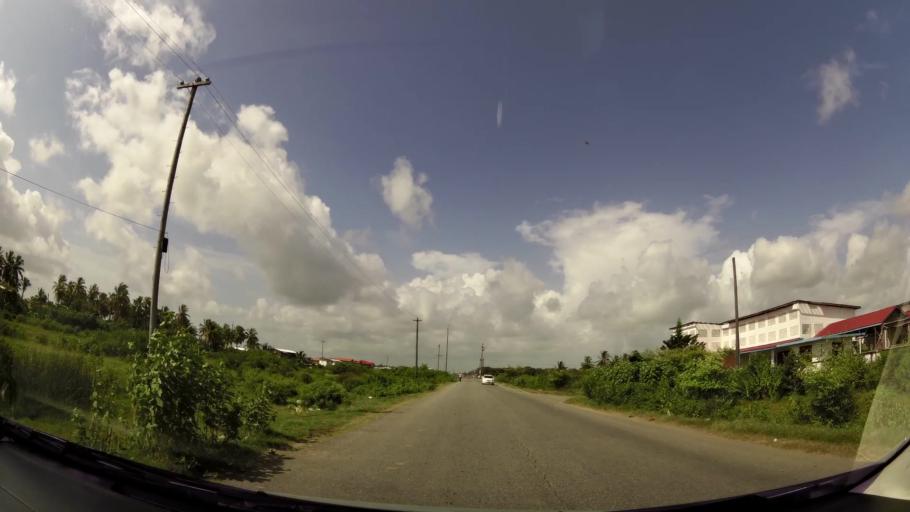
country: GY
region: Demerara-Mahaica
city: Mahaica Village
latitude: 6.7603
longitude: -57.9876
